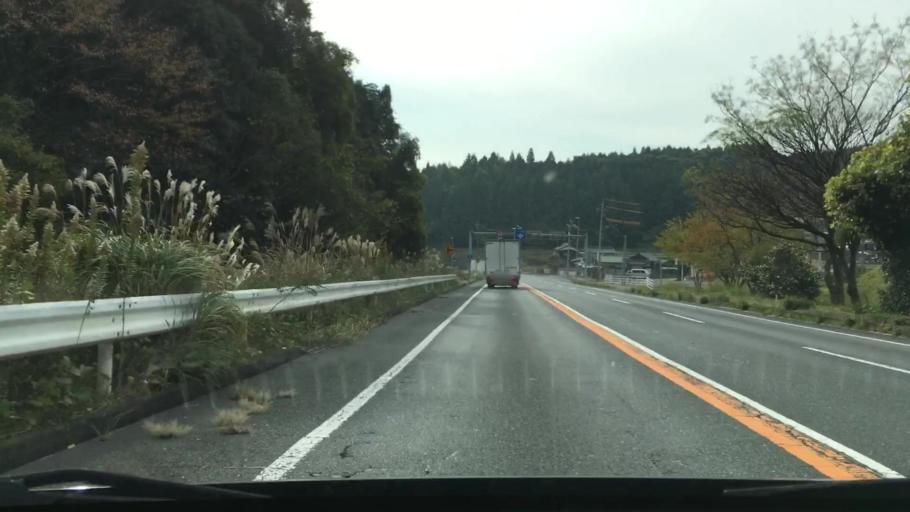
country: JP
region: Yamaguchi
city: Hikari
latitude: 34.0662
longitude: 131.9763
